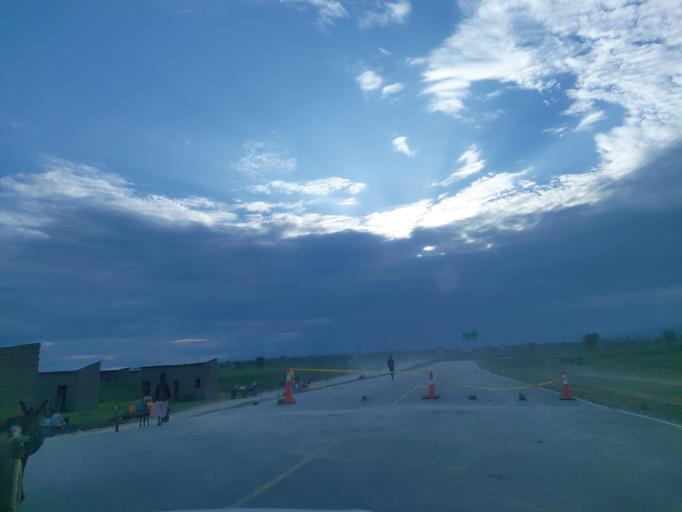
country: ET
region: Oromiya
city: Ziway
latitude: 8.1469
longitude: 38.8023
